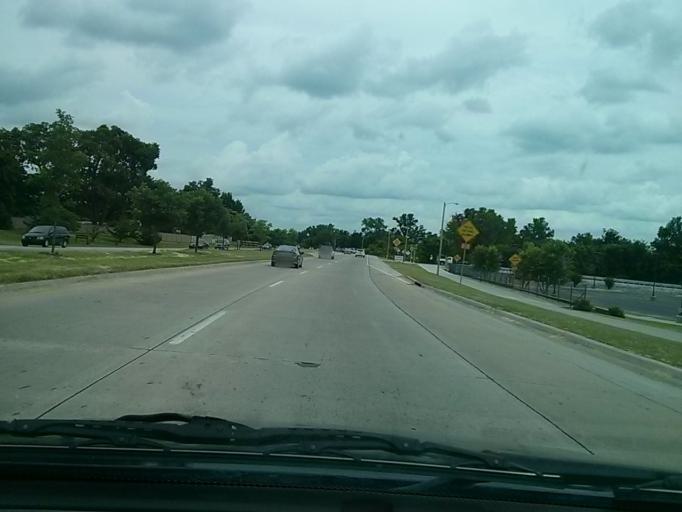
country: US
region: Oklahoma
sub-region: Tulsa County
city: Jenks
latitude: 36.0379
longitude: -95.9587
